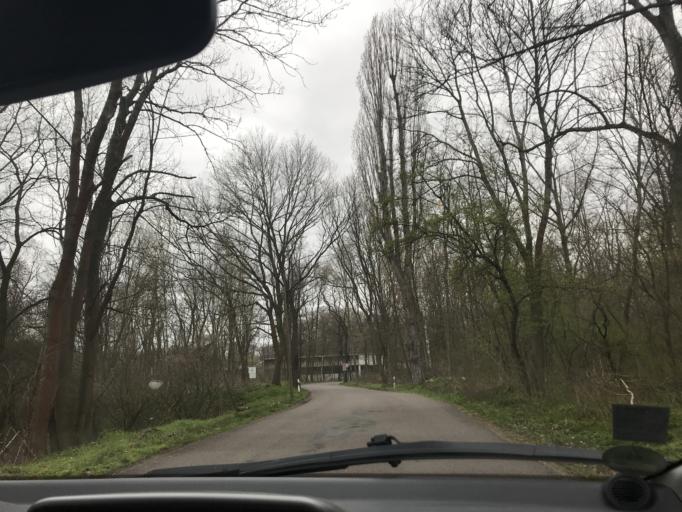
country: DE
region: Saxony
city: Schkeuditz
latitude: 51.3659
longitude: 12.2577
